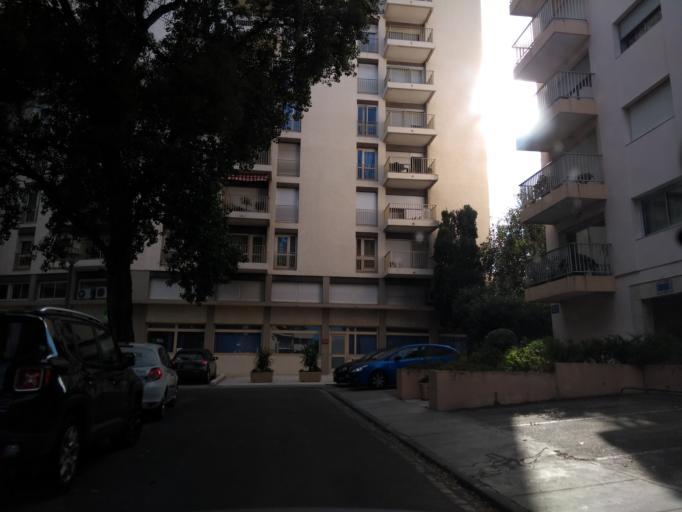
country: FR
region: Languedoc-Roussillon
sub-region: Departement des Pyrenees-Orientales
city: Perpignan
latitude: 42.6885
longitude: 2.9037
